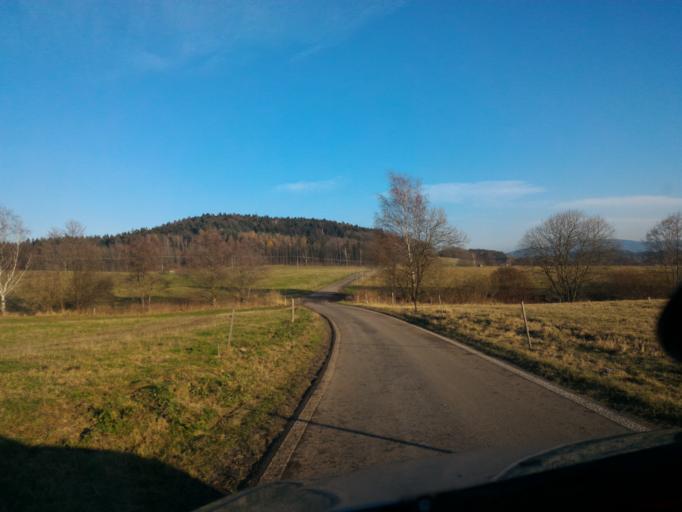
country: CZ
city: Jablonne v Podjestedi
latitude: 50.7952
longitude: 14.7485
